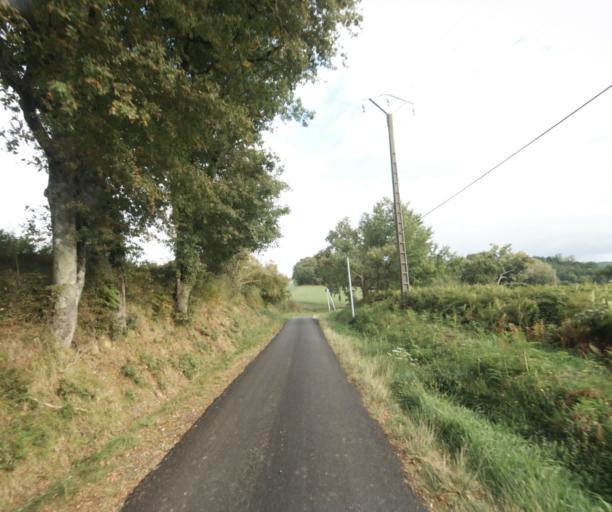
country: FR
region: Midi-Pyrenees
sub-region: Departement du Gers
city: Eauze
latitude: 43.8759
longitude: 0.1093
